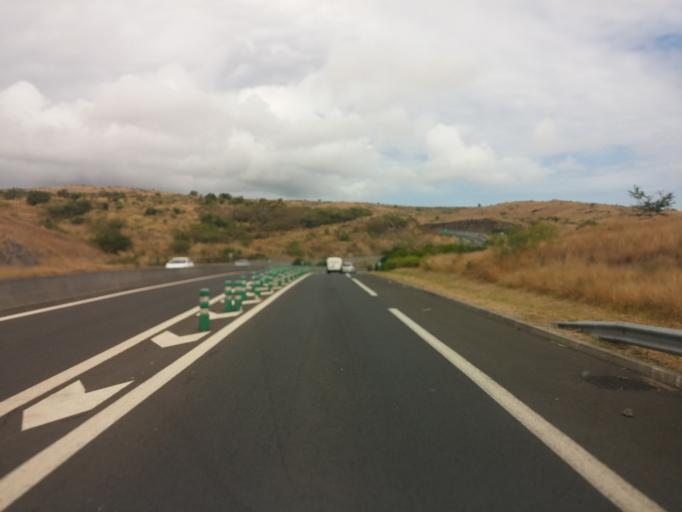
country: RE
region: Reunion
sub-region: Reunion
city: Saint-Paul
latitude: -21.0206
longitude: 55.2579
